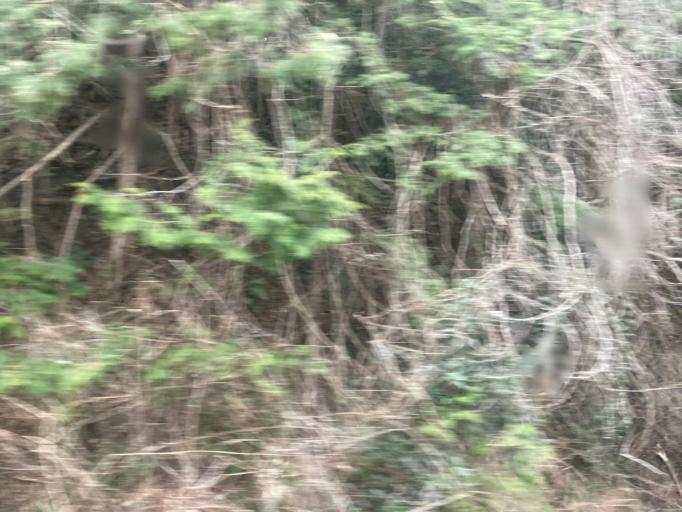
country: JP
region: Ibaraki
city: Daigo
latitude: 36.8338
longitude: 140.3828
